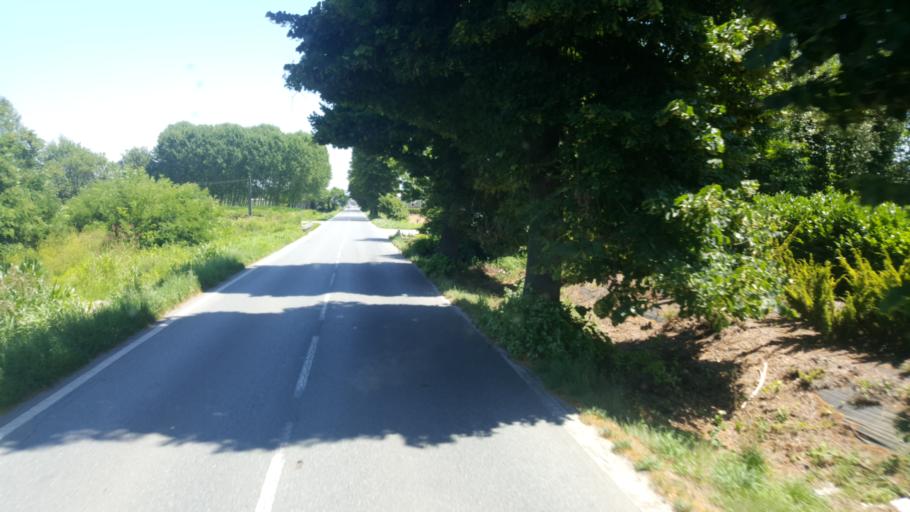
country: IT
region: Piedmont
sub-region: Provincia di Torino
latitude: 44.9249
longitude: 7.5137
